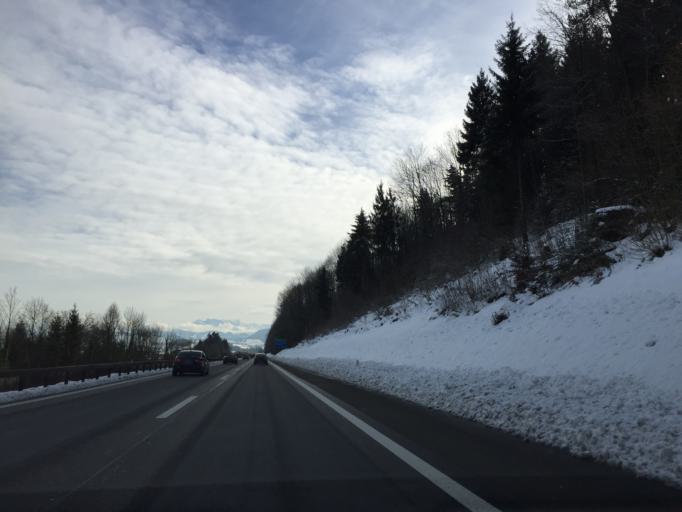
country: CH
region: Zurich
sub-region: Bezirk Horgen
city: Horgen / Allmend
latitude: 47.2475
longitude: 8.5987
